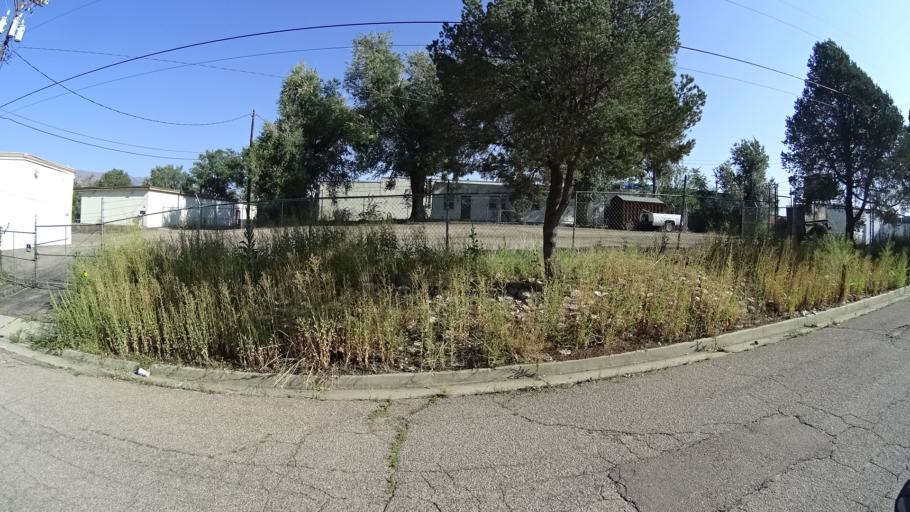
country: US
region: Colorado
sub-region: El Paso County
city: Colorado Springs
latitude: 38.8750
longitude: -104.8295
